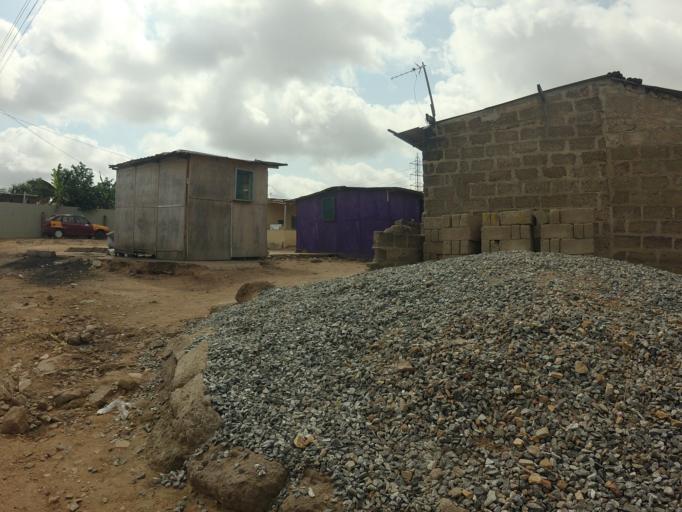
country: GH
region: Greater Accra
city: Dome
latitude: 5.6178
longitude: -0.2460
